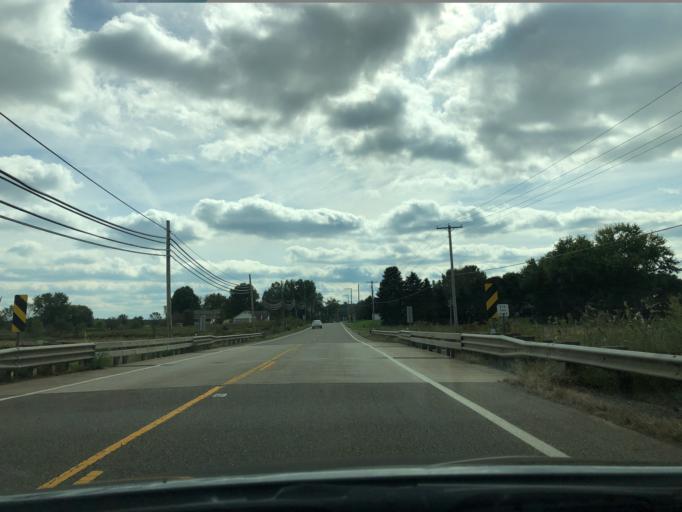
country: US
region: Ohio
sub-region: Stark County
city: Brewster
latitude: 40.6905
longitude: -81.5990
